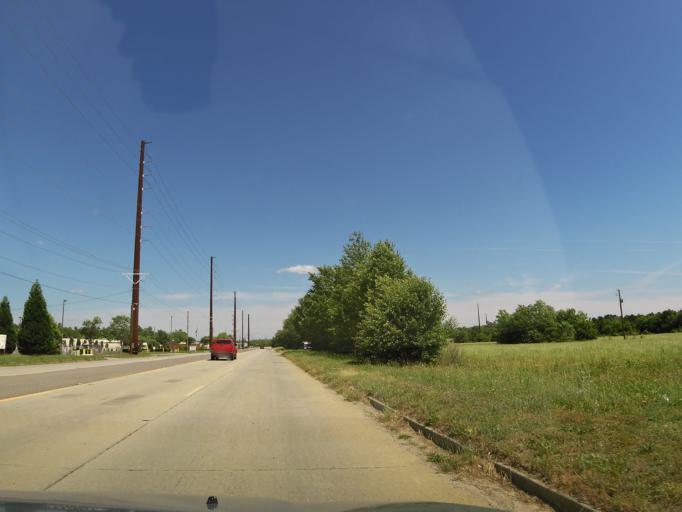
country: US
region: South Carolina
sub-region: Aiken County
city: Aiken
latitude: 33.5521
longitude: -81.6938
